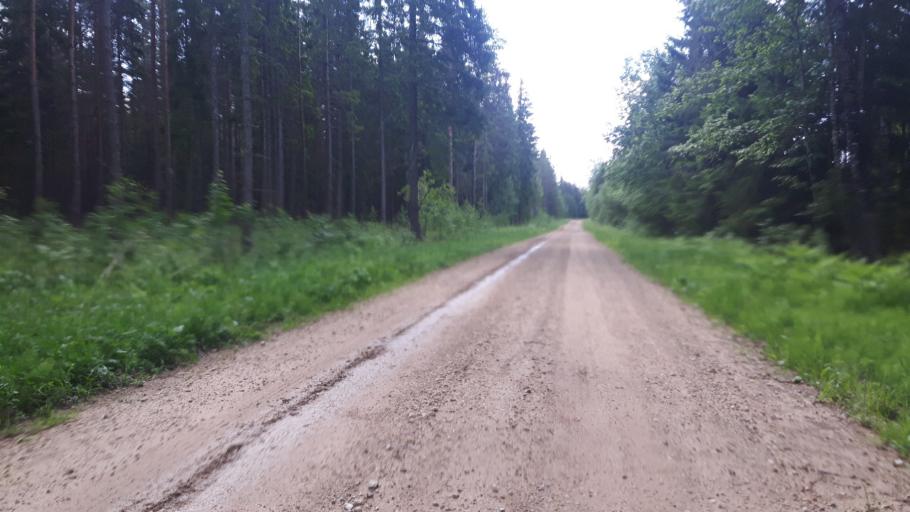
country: EE
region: Paernumaa
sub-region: Vaendra vald (alev)
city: Vandra
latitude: 58.7263
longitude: 25.0335
